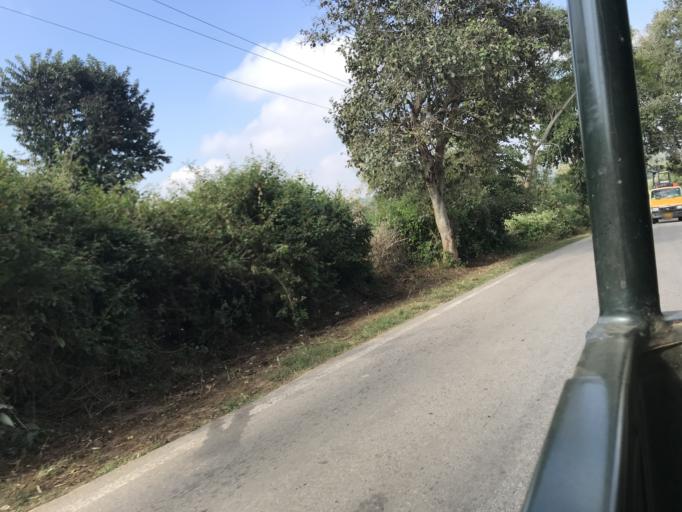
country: IN
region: Karnataka
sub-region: Mysore
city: Heggadadevankote
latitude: 11.9467
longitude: 76.2529
